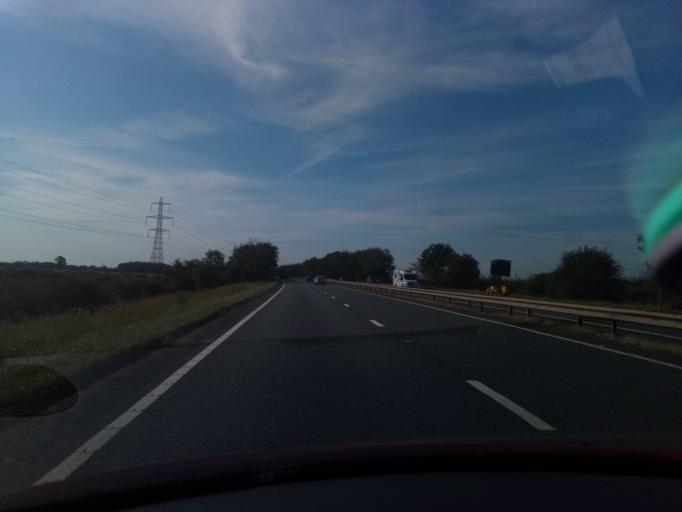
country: GB
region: England
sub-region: Stockton-on-Tees
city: Yarm
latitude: 54.4784
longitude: -1.3167
